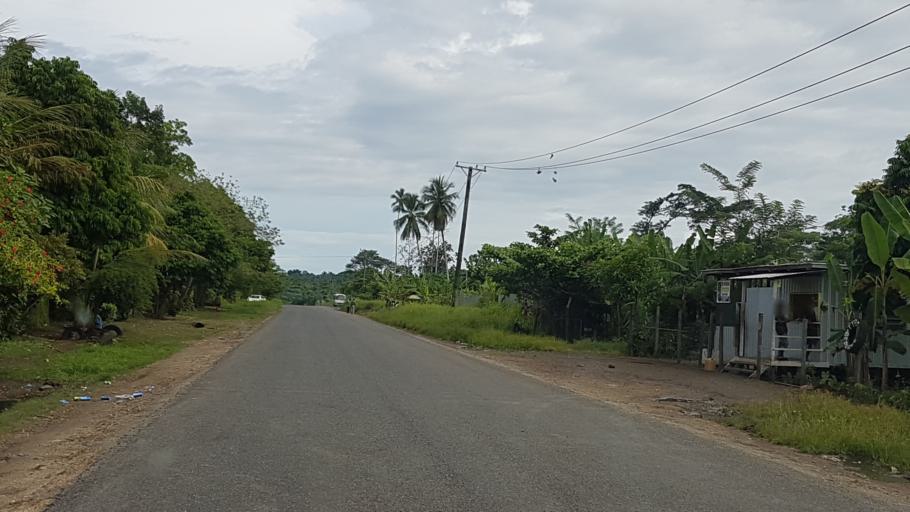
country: PG
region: Madang
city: Madang
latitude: -5.1622
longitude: 145.7792
